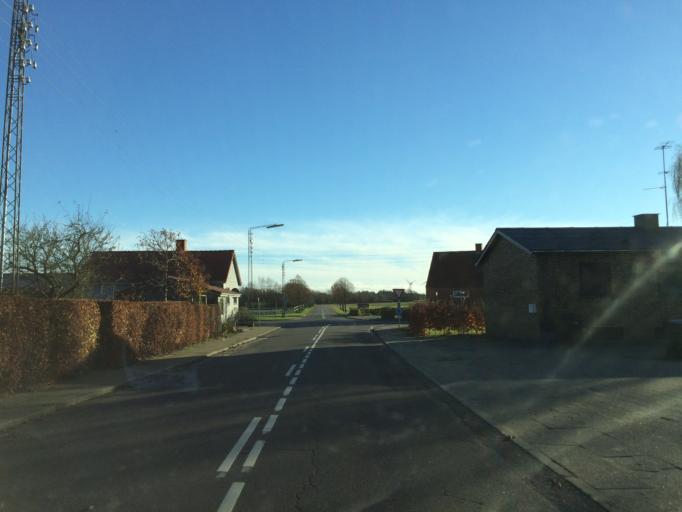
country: DK
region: Central Jutland
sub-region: Ringkobing-Skjern Kommune
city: Videbaek
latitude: 56.1671
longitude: 8.6157
